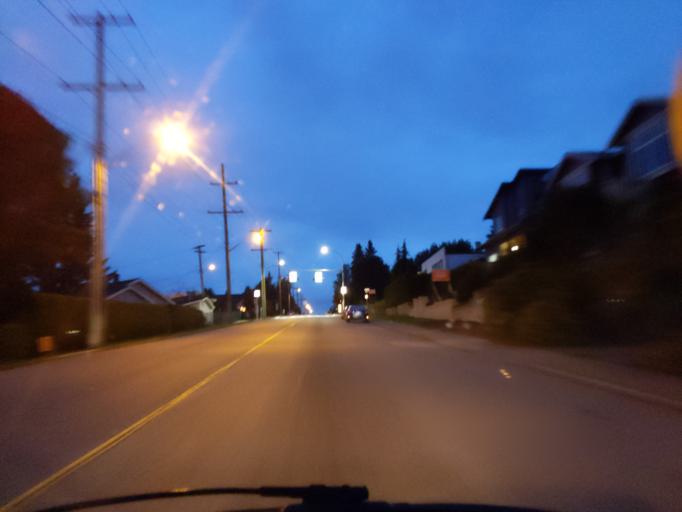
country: CA
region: British Columbia
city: New Westminster
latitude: 49.2287
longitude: -122.9001
